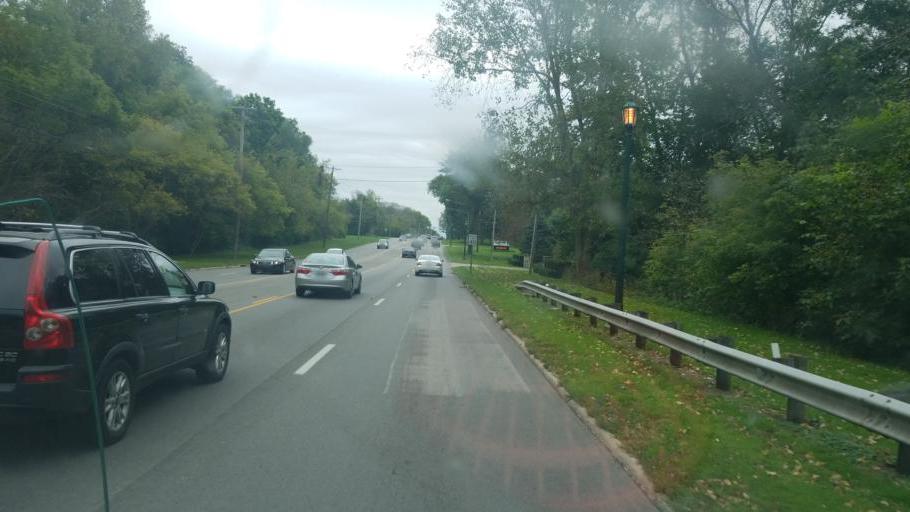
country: US
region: Ohio
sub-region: Lucas County
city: Ottawa Hills
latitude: 41.6769
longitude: -83.6592
